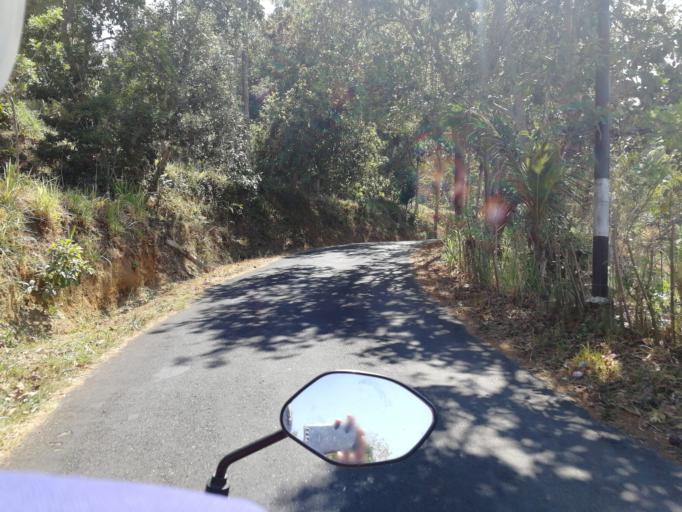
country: ID
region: Bali
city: Banjar Kedisan
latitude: -8.1551
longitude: 115.3073
